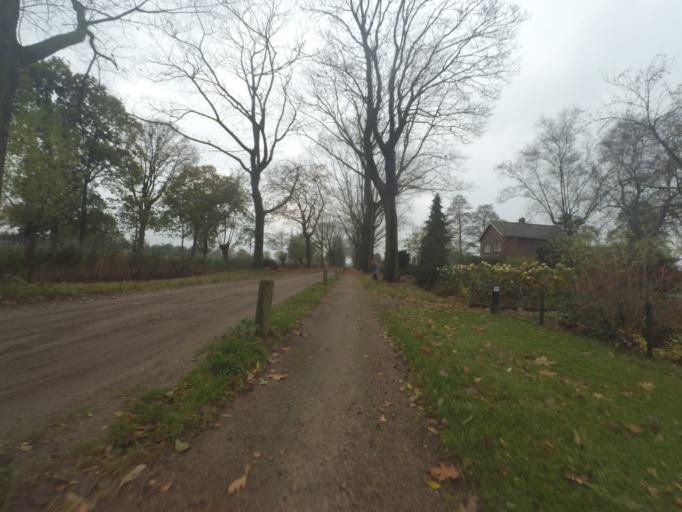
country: NL
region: Gelderland
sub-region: Gemeente Ede
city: Lunteren
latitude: 52.0637
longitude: 5.6232
